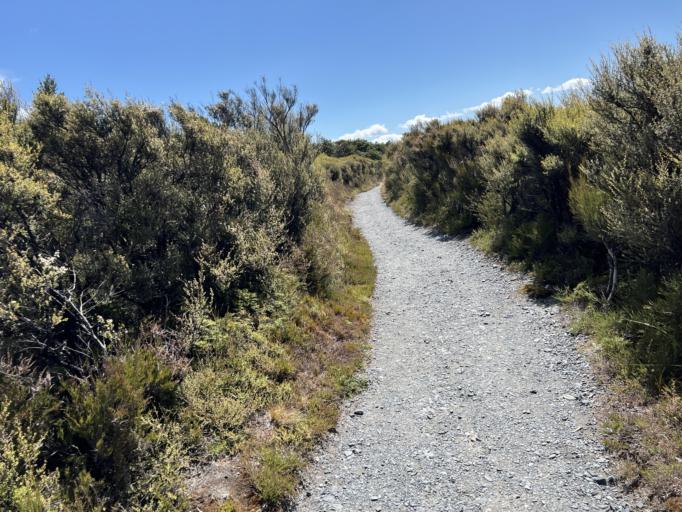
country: NZ
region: Manawatu-Wanganui
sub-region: Ruapehu District
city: Waiouru
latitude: -39.2005
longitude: 175.5507
